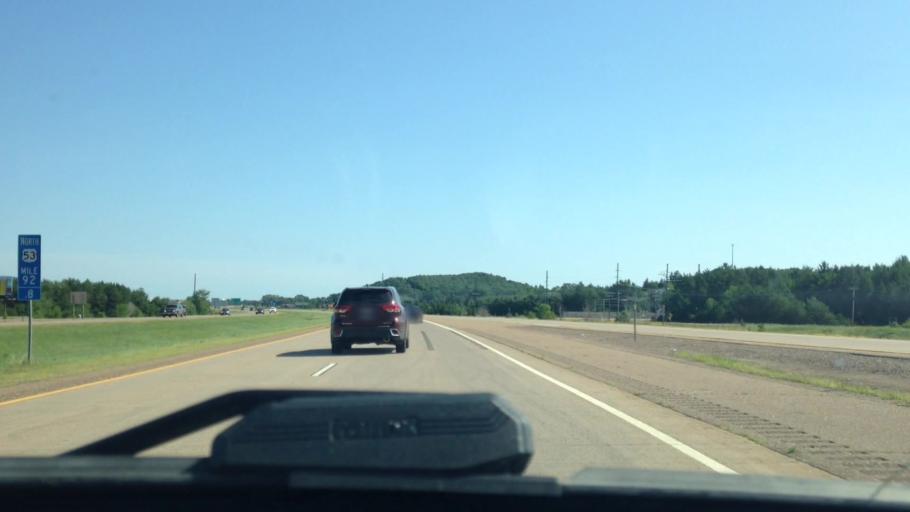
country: US
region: Wisconsin
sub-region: Chippewa County
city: Lake Hallie
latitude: 44.8635
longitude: -91.4250
